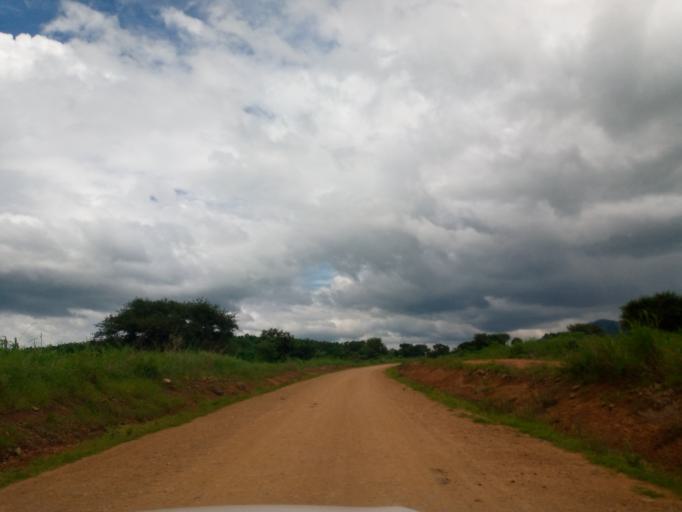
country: ET
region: Oromiya
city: Mendi
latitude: 10.1946
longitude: 35.0926
